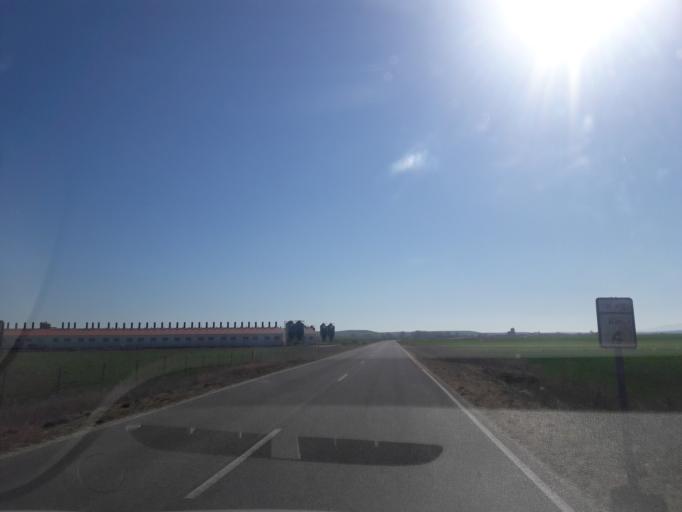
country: ES
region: Castille and Leon
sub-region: Provincia de Salamanca
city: Salmoral
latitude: 40.8093
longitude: -5.2426
